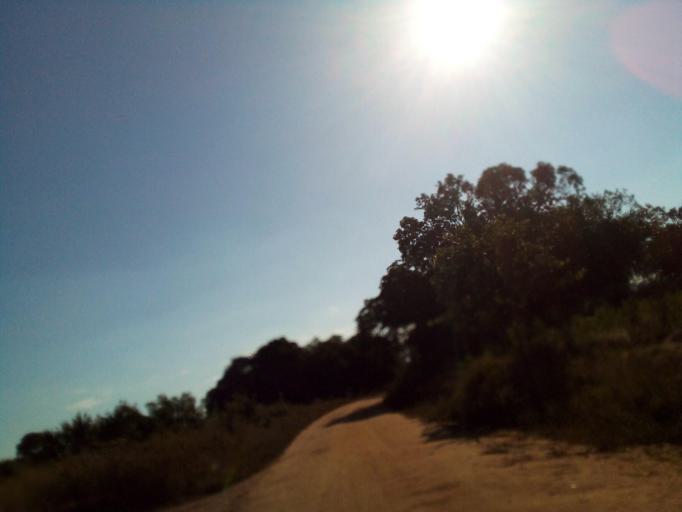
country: MZ
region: Zambezia
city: Quelimane
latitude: -17.5090
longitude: 36.5924
